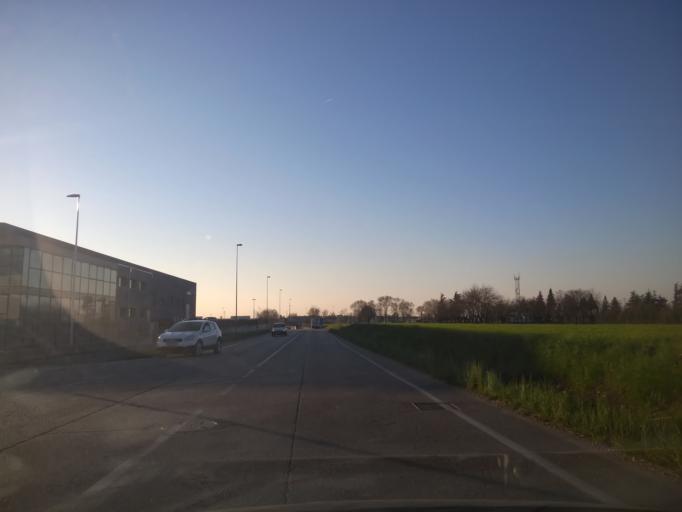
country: IT
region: Veneto
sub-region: Provincia di Vicenza
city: Thiene
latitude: 45.6868
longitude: 11.4628
